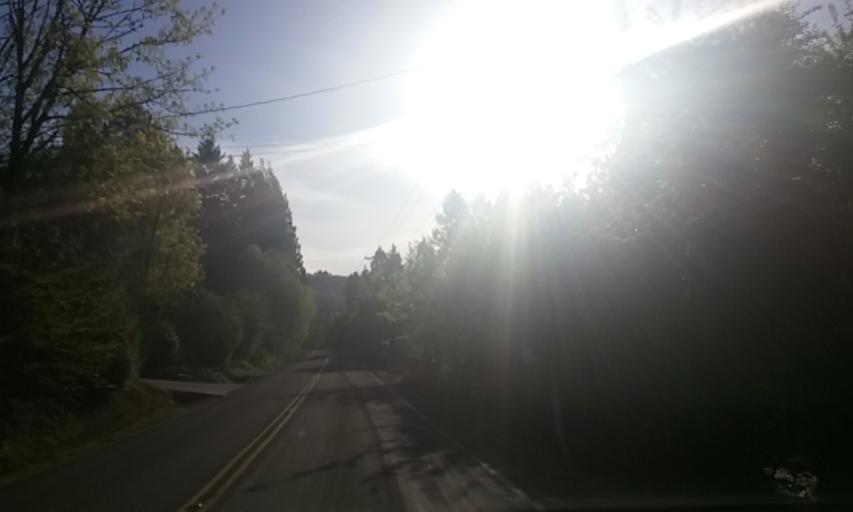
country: US
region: Oregon
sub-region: Washington County
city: Cedar Mill
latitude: 45.5435
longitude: -122.7870
